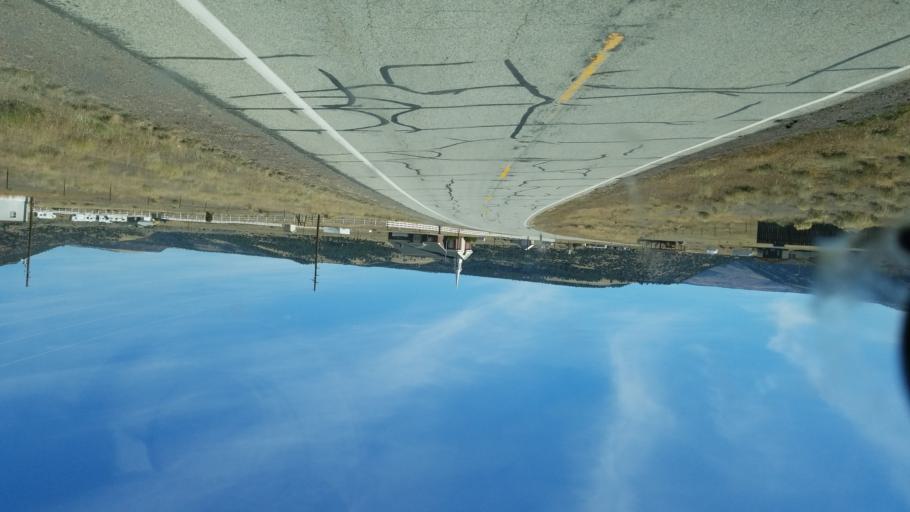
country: US
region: Colorado
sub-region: Conejos County
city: Conejos
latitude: 37.0662
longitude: -106.1979
